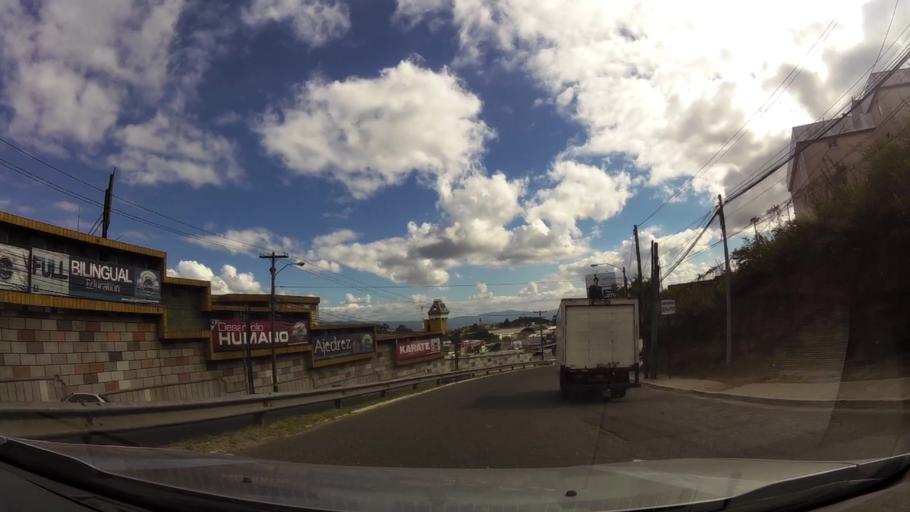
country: GT
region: Guatemala
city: Mixco
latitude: 14.6160
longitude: -90.6053
